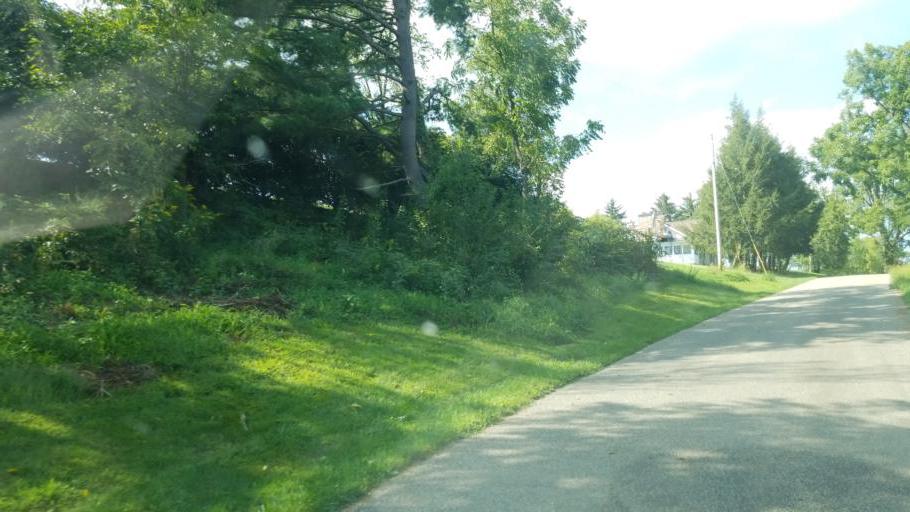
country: US
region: Ohio
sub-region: Knox County
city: Danville
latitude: 40.4421
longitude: -82.3089
